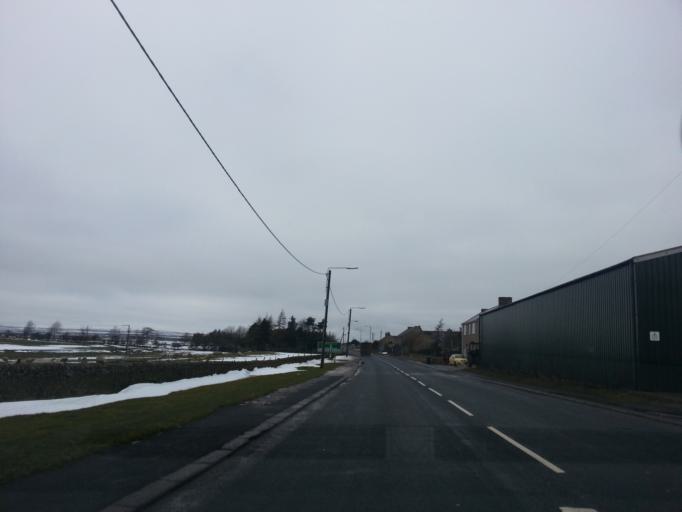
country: GB
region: England
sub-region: County Durham
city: Tow Law
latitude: 54.7521
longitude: -1.8249
